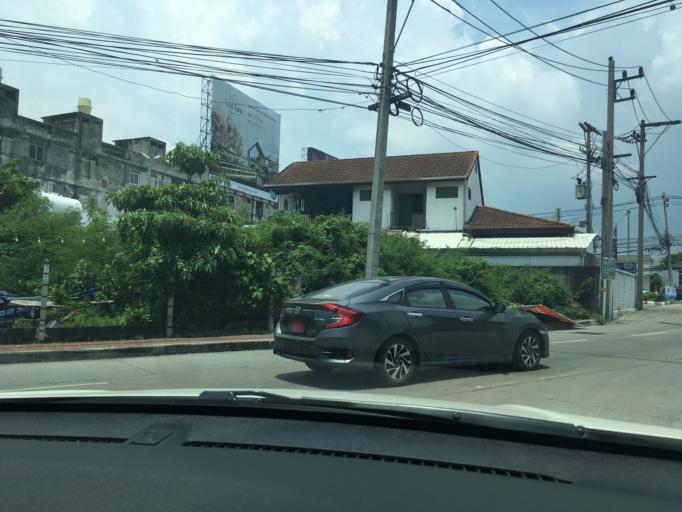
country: TH
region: Chon Buri
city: Chon Buri
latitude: 13.3547
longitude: 100.9825
